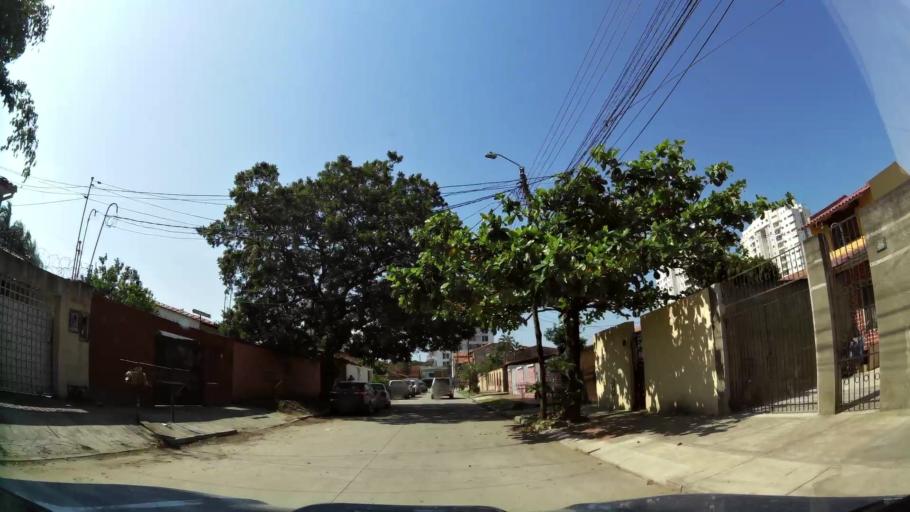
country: BO
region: Santa Cruz
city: Santa Cruz de la Sierra
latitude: -17.7469
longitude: -63.1698
